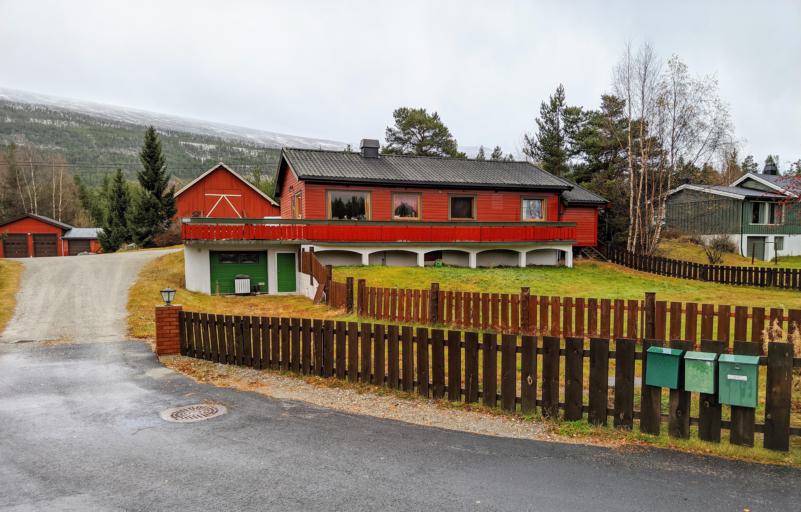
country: NO
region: Oppland
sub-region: Skjak
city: Bismo
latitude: 61.9122
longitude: 8.1122
